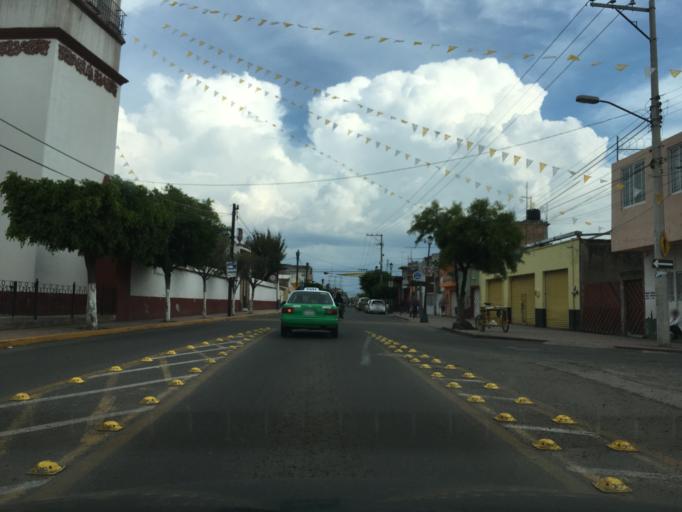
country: MX
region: Guanajuato
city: Celaya
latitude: 20.5309
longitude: -100.8187
